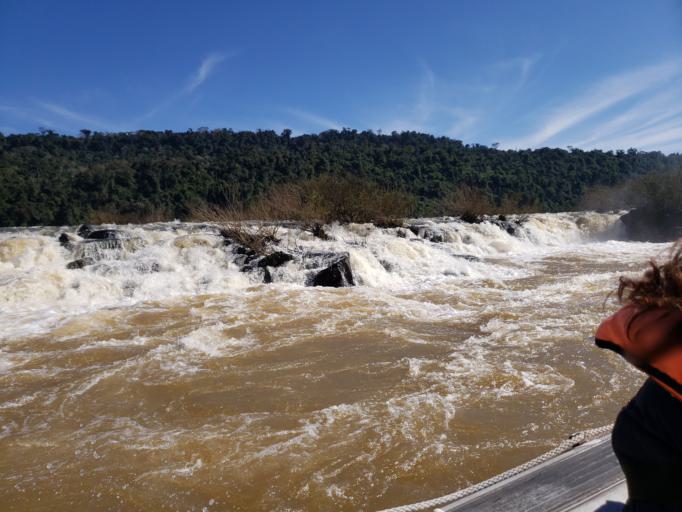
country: BR
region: Rio Grande do Sul
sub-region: Tres Passos
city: Tres Passos
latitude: -27.1468
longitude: -53.8867
